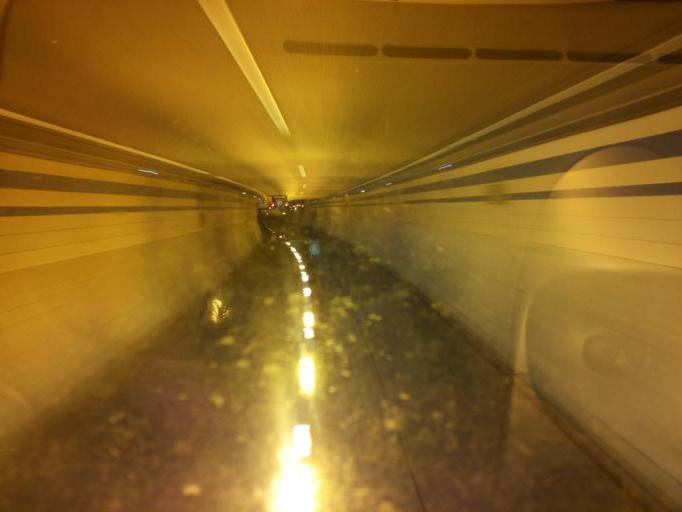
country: CH
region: Lucerne
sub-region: Sursee District
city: Eich
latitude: 47.1483
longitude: 8.1742
